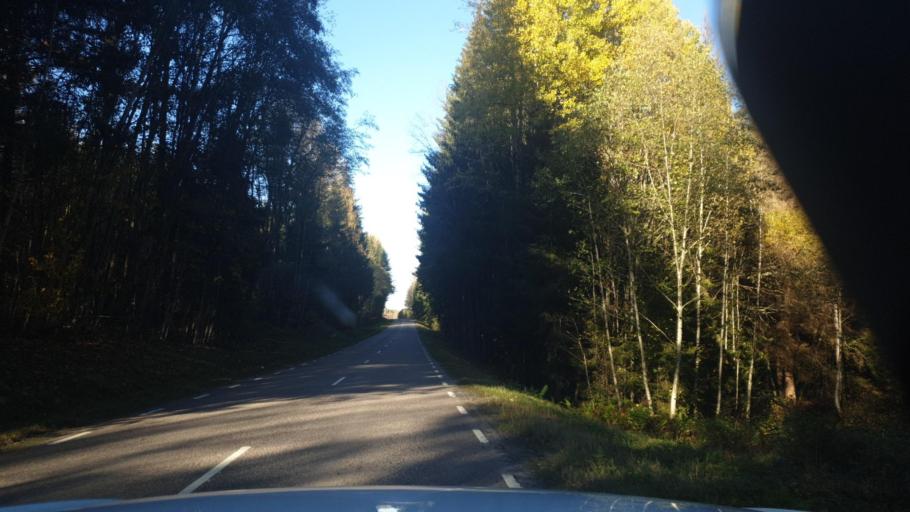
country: SE
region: Vaermland
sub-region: Arvika Kommun
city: Arvika
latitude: 59.6293
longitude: 12.8876
